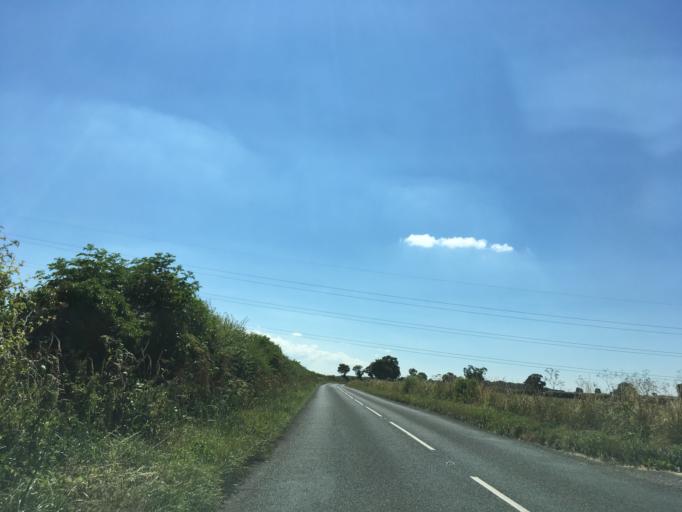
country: GB
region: England
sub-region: South Gloucestershire
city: Marshfield
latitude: 51.5150
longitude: -2.3148
